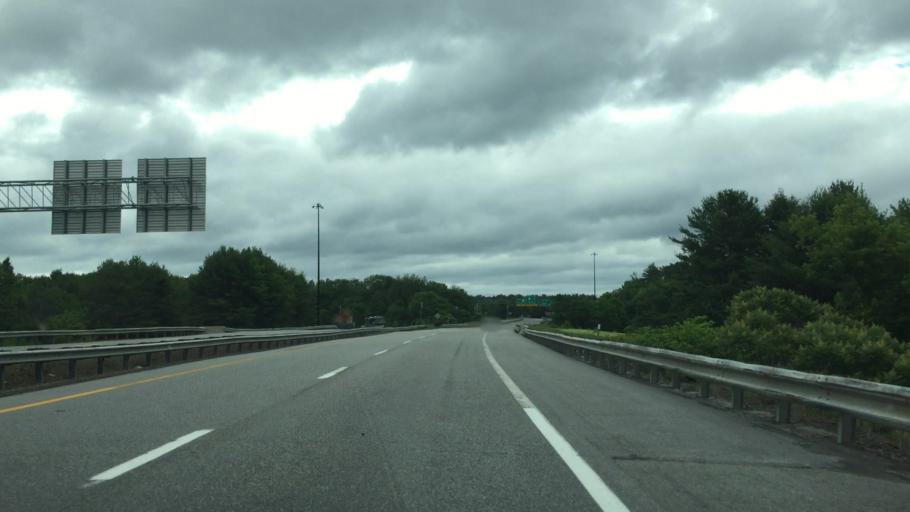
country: US
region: Maine
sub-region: Cumberland County
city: Falmouth
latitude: 43.7327
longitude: -70.2349
